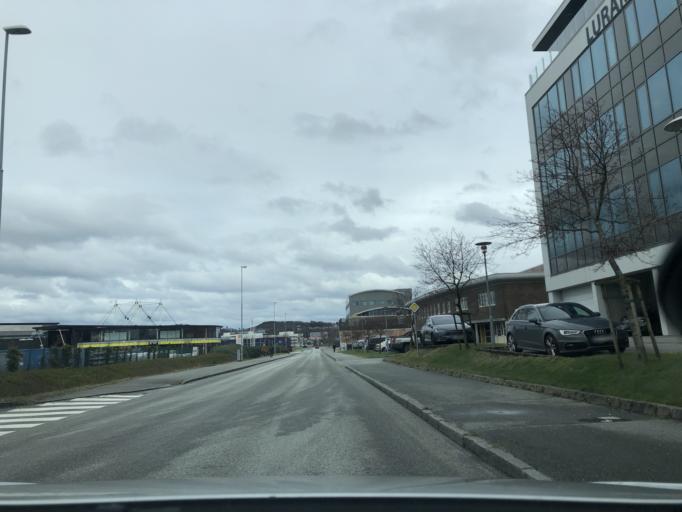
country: NO
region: Rogaland
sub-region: Sandnes
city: Sandnes
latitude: 58.8822
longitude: 5.7214
